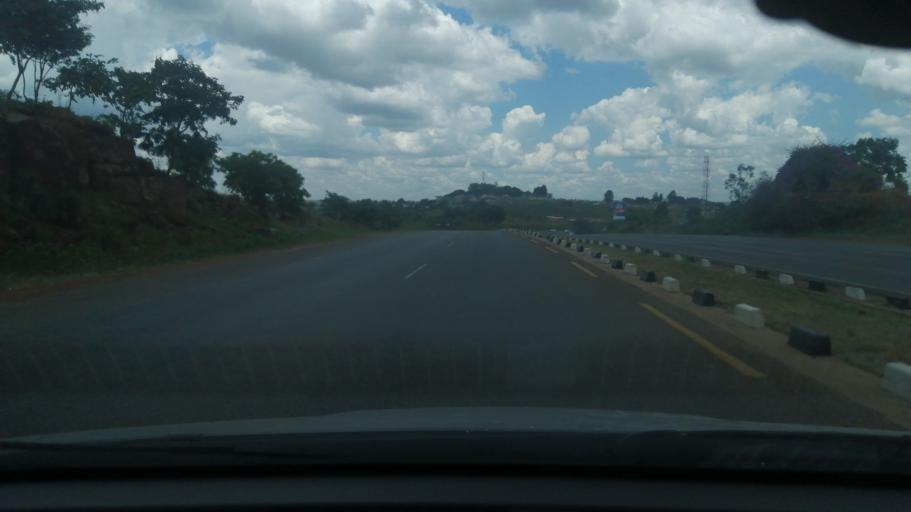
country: ZW
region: Harare
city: Harare
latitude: -17.8184
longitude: 30.9308
